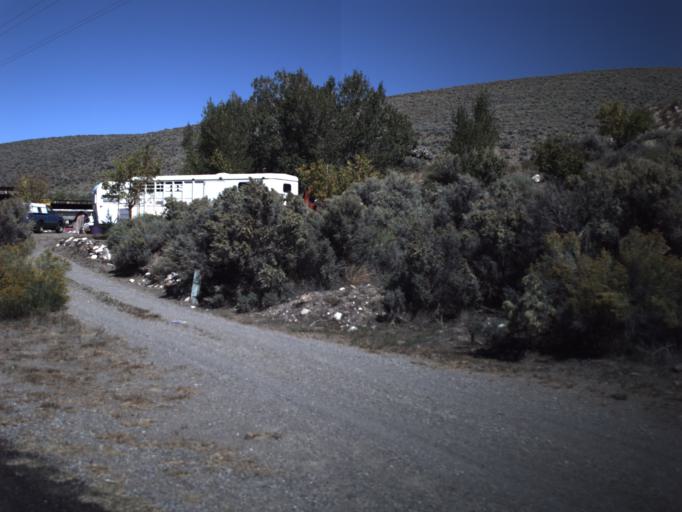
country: US
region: Utah
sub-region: Piute County
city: Junction
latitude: 38.1052
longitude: -111.9855
